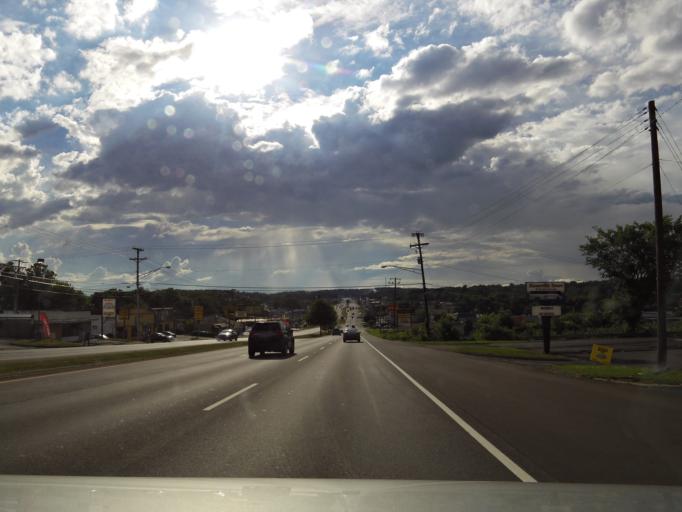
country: US
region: Tennessee
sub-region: Knox County
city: Knoxville
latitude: 36.0021
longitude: -83.9746
